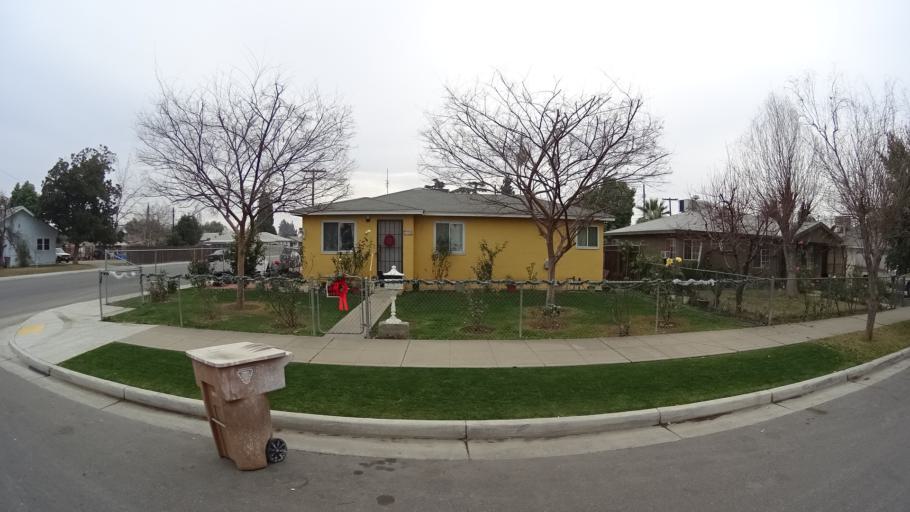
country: US
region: California
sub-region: Kern County
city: Bakersfield
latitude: 35.3719
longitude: -118.9866
